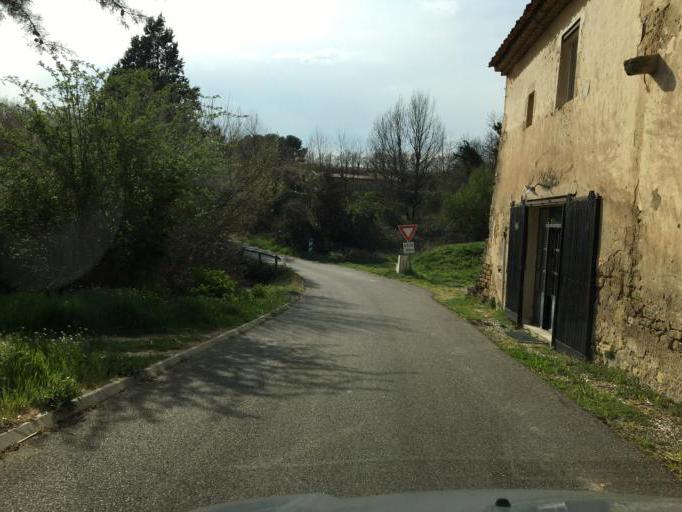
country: FR
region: Provence-Alpes-Cote d'Azur
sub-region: Departement du Vaucluse
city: Ansouis
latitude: 43.7371
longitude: 5.4617
